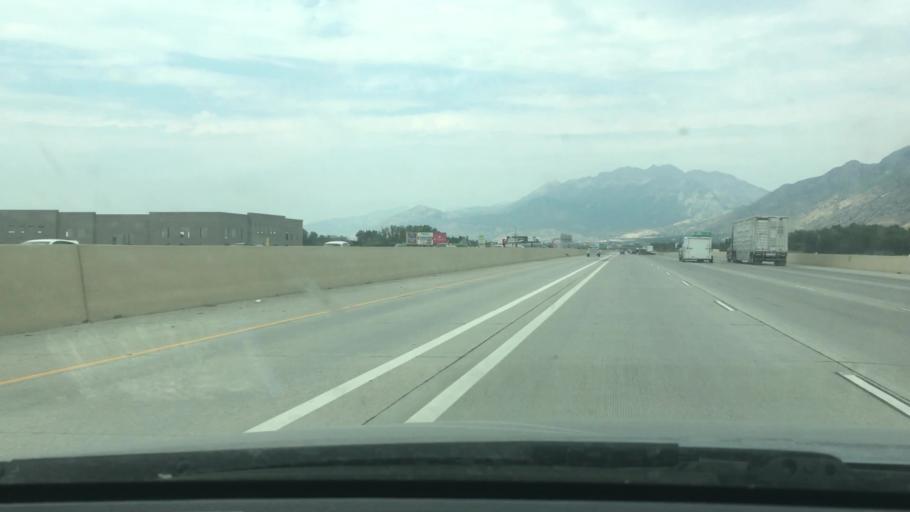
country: US
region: Utah
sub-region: Utah County
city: Springville
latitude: 40.1743
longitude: -111.6465
